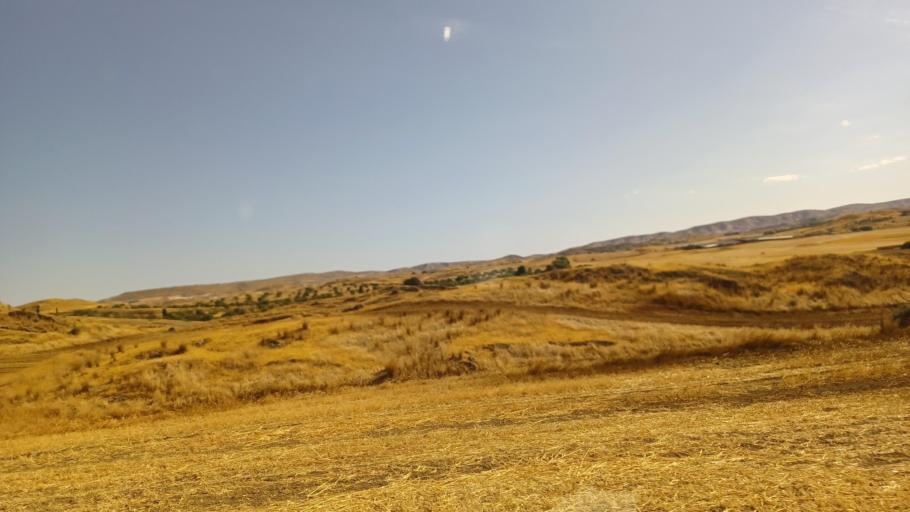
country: CY
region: Larnaka
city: Troulloi
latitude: 35.0049
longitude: 33.5907
